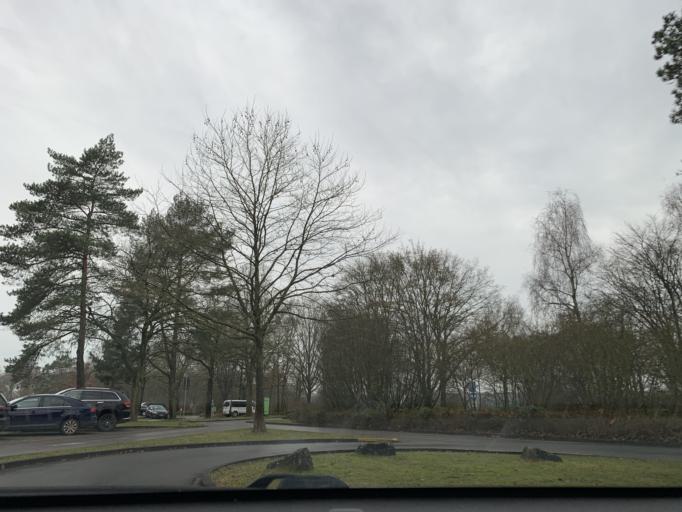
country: DE
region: North Rhine-Westphalia
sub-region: Regierungsbezirk Munster
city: Muenster
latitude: 51.9488
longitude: 7.5870
